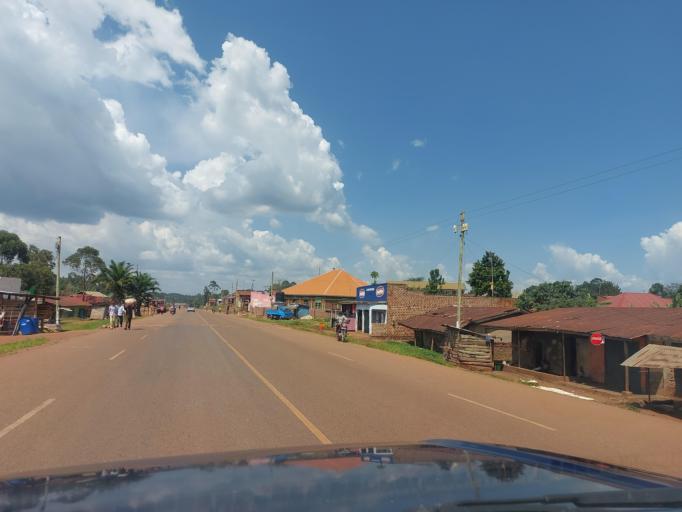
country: UG
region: Central Region
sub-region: Buikwe District
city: Njeru
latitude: 0.3888
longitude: 33.1666
